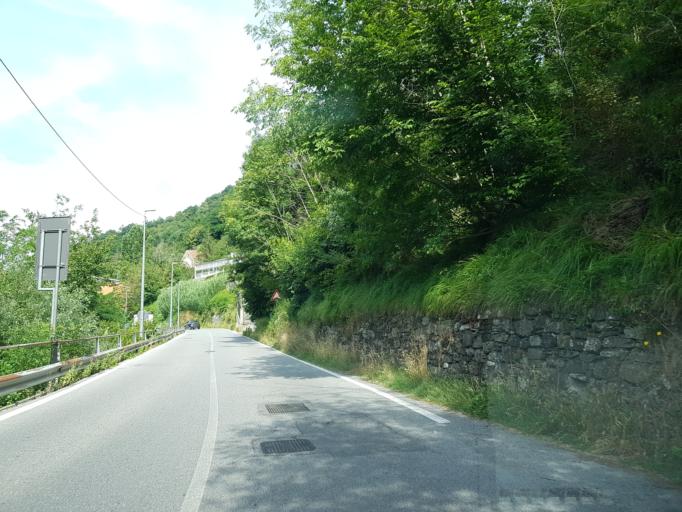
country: IT
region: Liguria
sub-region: Provincia di Genova
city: Piccarello
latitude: 44.4838
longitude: 8.9605
